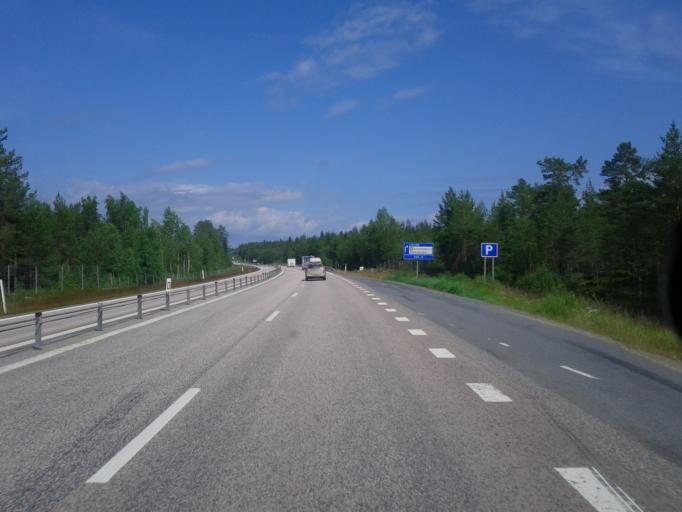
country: SE
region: Vaesternorrland
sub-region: OErnskoeldsviks Kommun
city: Husum
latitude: 63.3701
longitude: 19.1888
